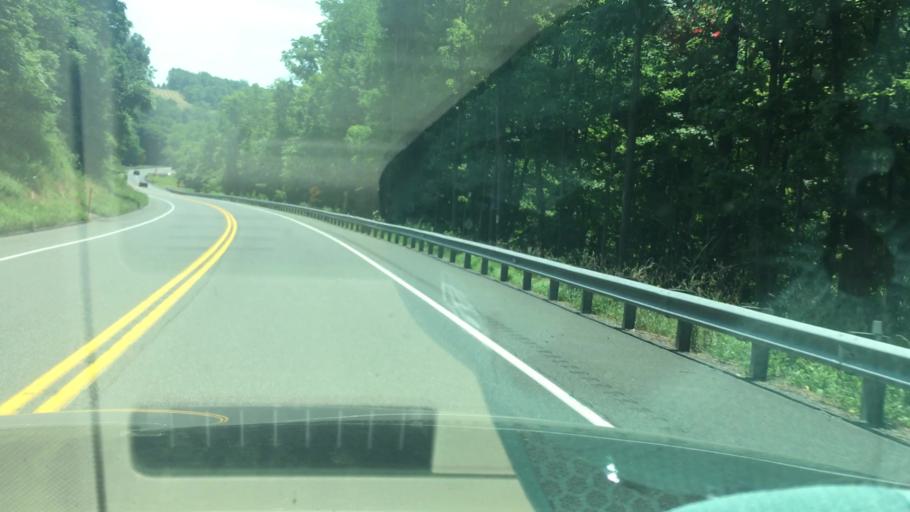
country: US
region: Pennsylvania
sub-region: Lehigh County
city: Schnecksville
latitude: 40.6605
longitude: -75.6866
